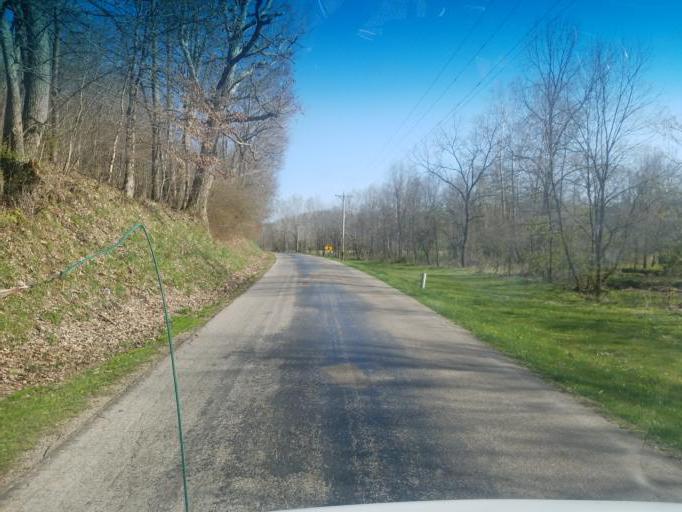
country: US
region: Ohio
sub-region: Muskingum County
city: Frazeysburg
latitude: 40.2316
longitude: -82.1920
